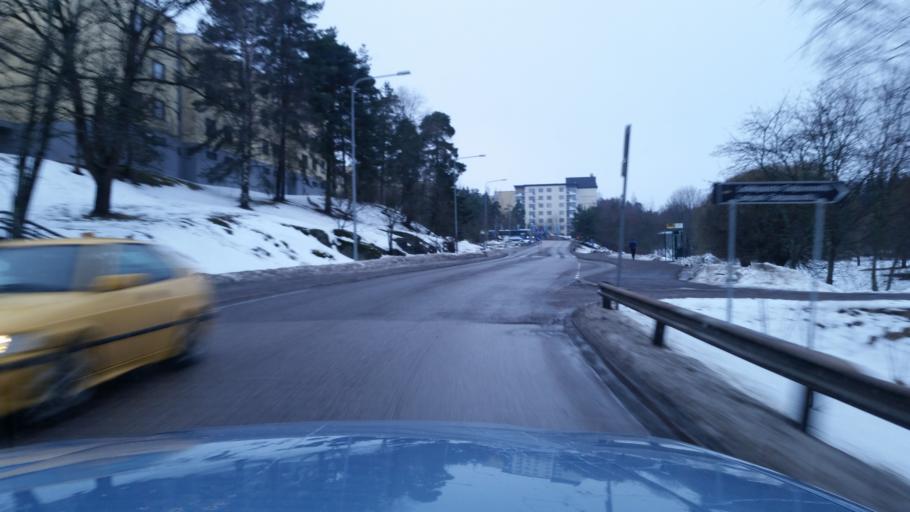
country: FI
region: Uusimaa
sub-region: Helsinki
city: Vantaa
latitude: 60.2303
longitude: 25.0056
